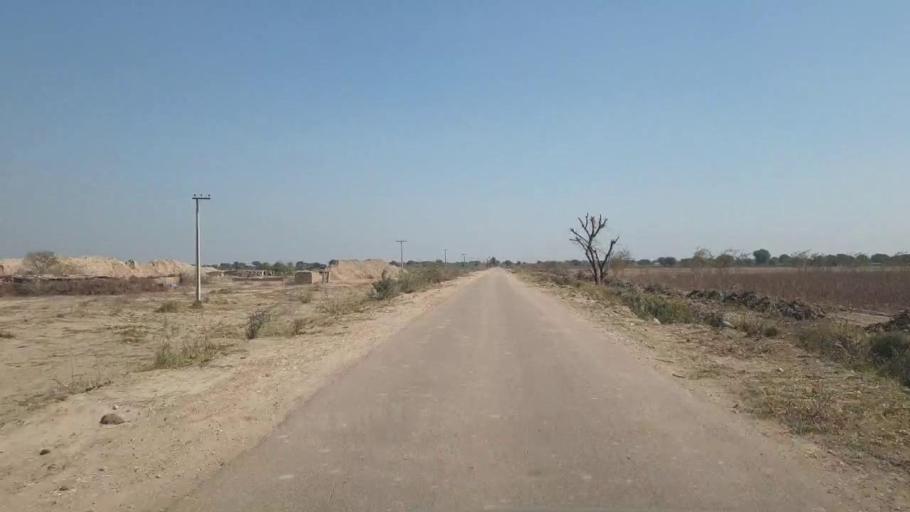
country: PK
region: Sindh
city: Chambar
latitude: 25.2885
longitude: 68.6662
